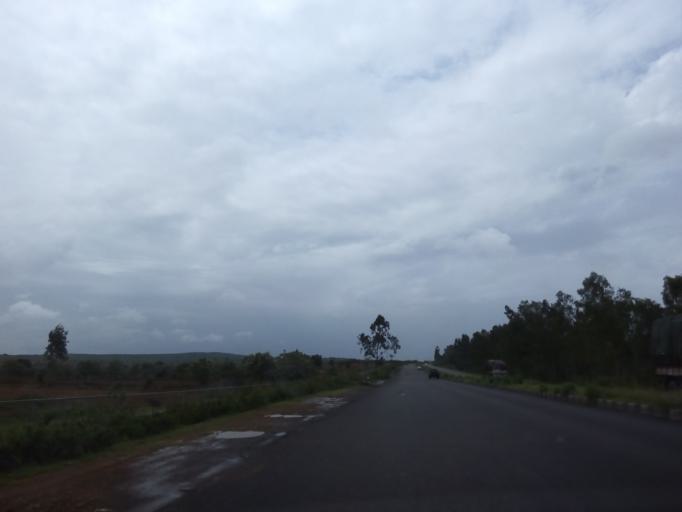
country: IN
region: Karnataka
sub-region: Haveri
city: Byadgi
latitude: 14.7113
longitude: 75.5057
